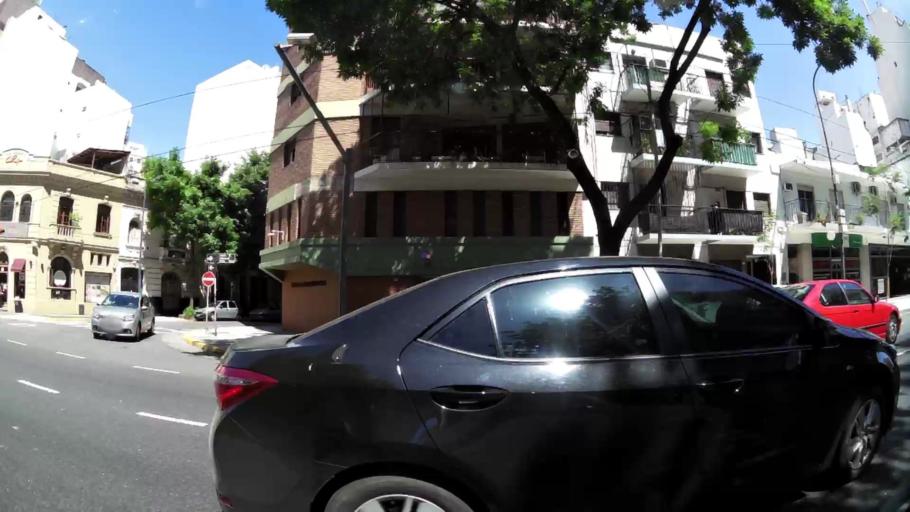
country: AR
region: Buenos Aires F.D.
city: Villa Santa Rita
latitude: -34.6244
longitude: -58.4460
